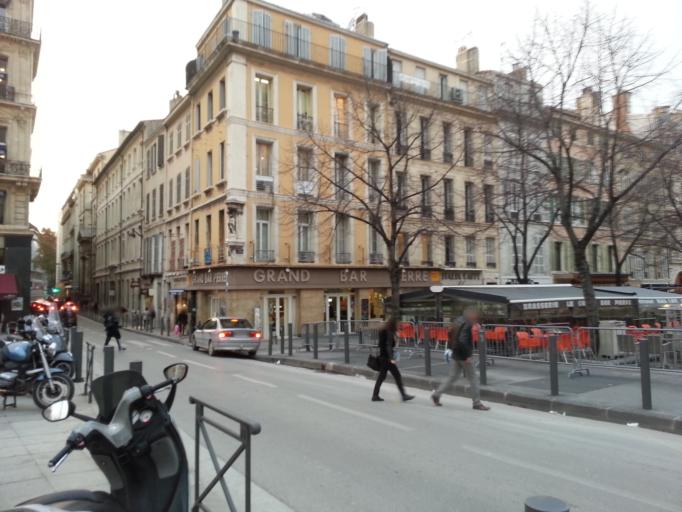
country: FR
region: Provence-Alpes-Cote d'Azur
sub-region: Departement des Bouches-du-Rhone
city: Marseille 06
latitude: 43.2909
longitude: 5.3798
